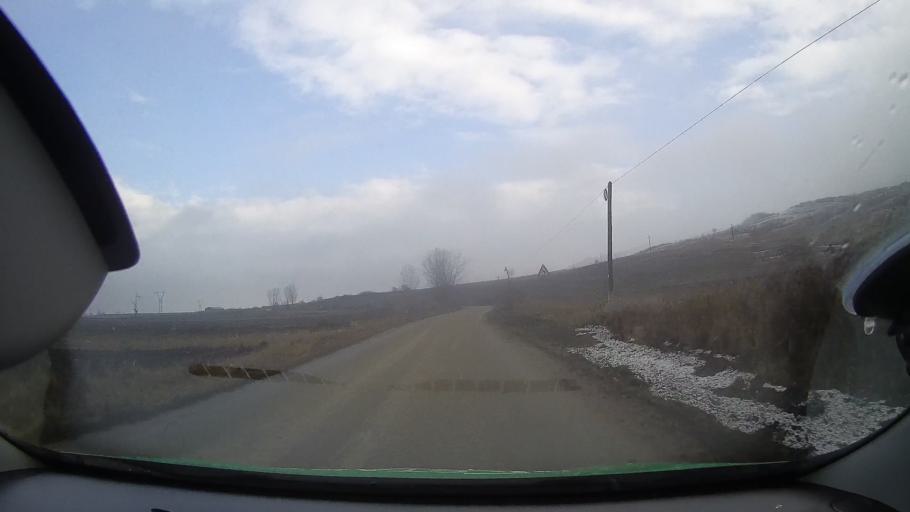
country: RO
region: Alba
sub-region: Comuna Noslac
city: Noslac
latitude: 46.4146
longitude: 23.9665
